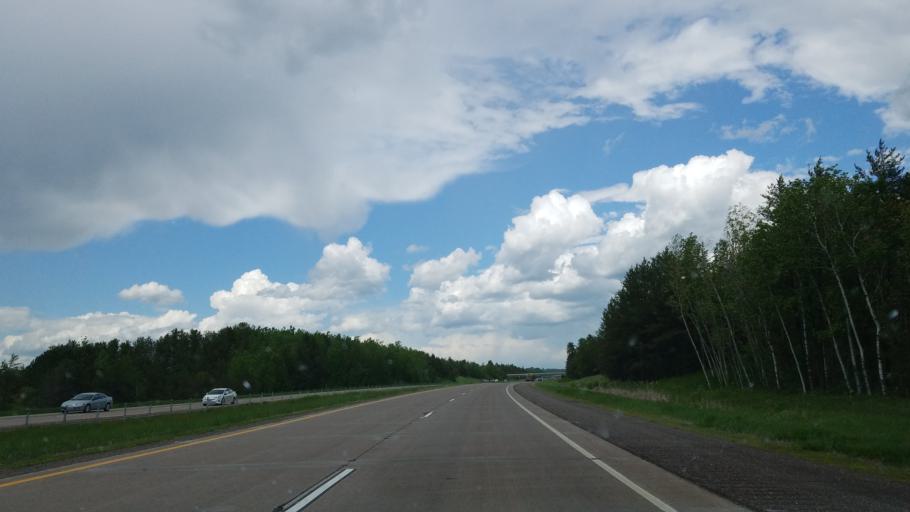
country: US
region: Minnesota
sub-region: Carlton County
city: Moose Lake
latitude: 46.4858
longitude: -92.7060
